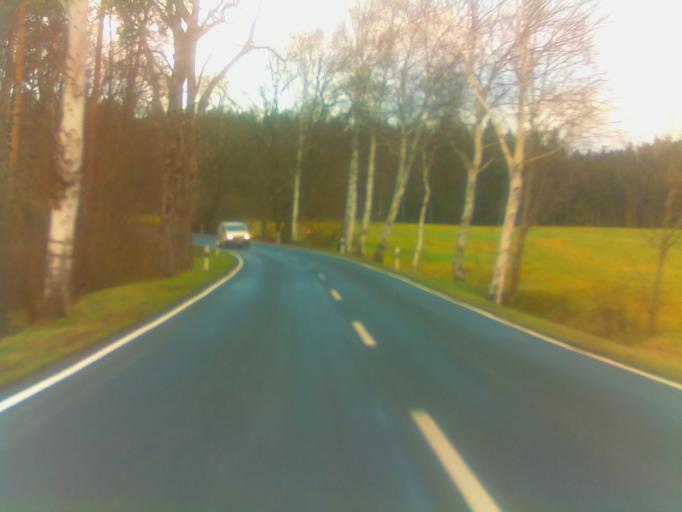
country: DE
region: Thuringia
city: Neustadt (Orla)
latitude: 50.7483
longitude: 11.7237
